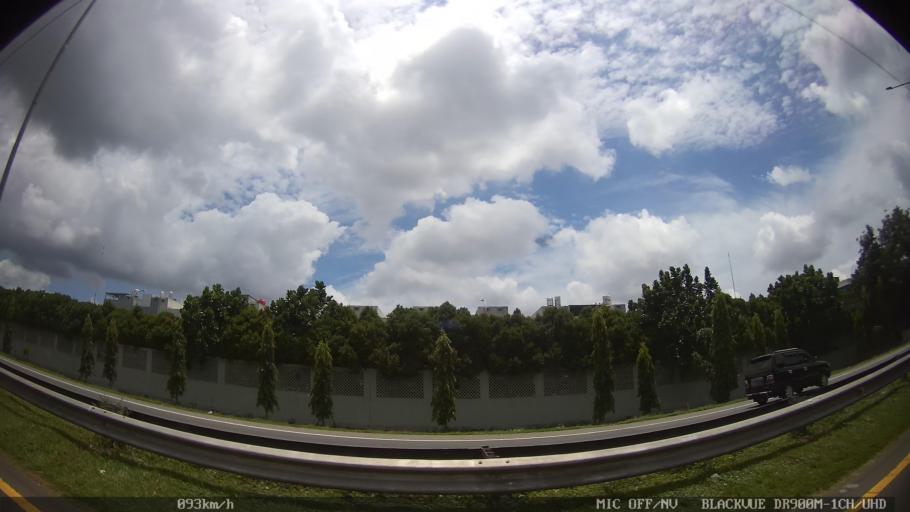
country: ID
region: North Sumatra
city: Medan
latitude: 3.6073
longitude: 98.7225
